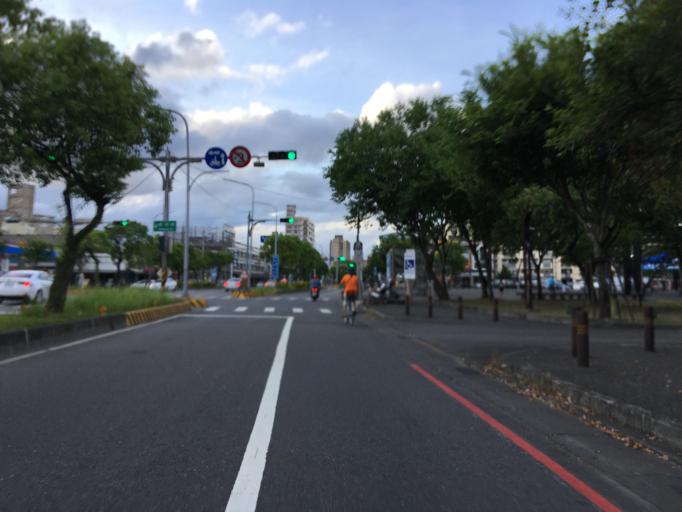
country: TW
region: Taiwan
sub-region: Yilan
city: Yilan
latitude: 24.6715
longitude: 121.7641
